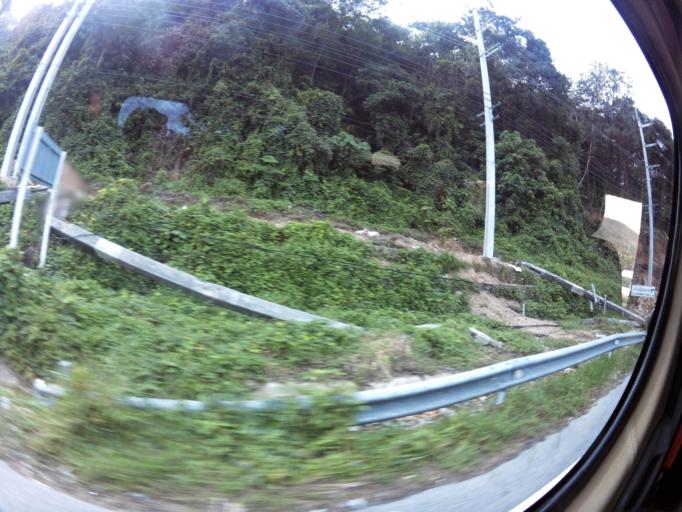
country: TH
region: Phuket
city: Patong
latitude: 7.9422
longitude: 98.2775
